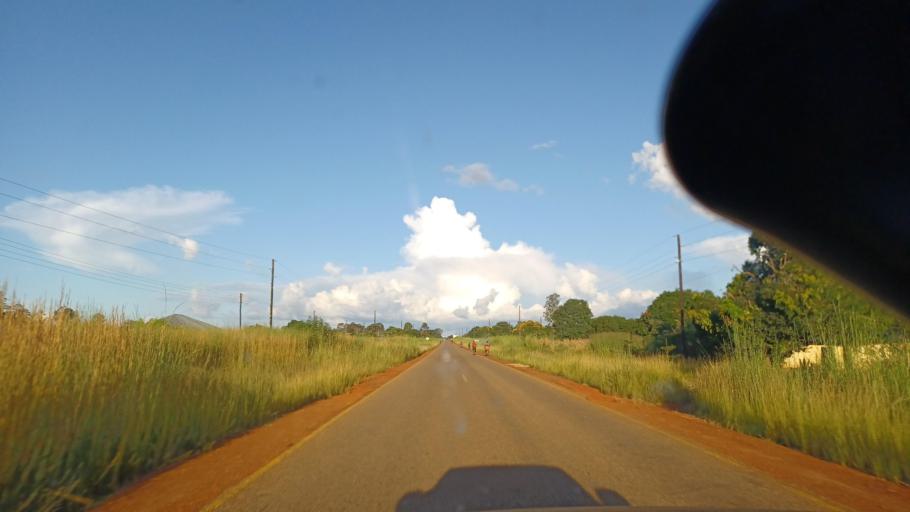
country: ZM
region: North-Western
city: Kalengwa
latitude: -13.1431
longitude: 25.0360
